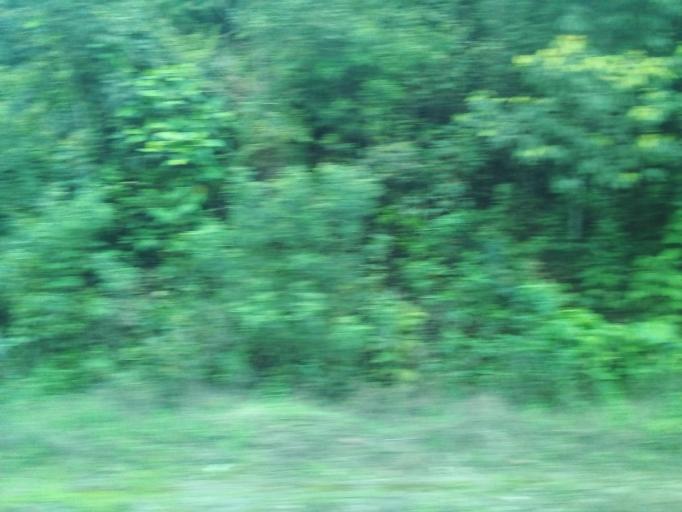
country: BR
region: Minas Gerais
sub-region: Rio Piracicaba
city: Rio Piracicaba
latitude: -19.9633
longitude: -43.2655
